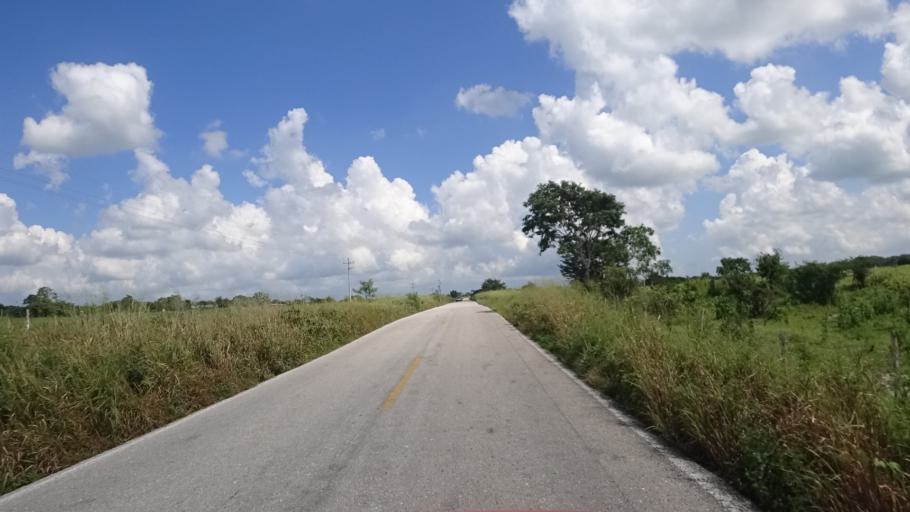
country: MX
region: Yucatan
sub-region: Panaba
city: Loche
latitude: 21.4355
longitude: -88.1407
